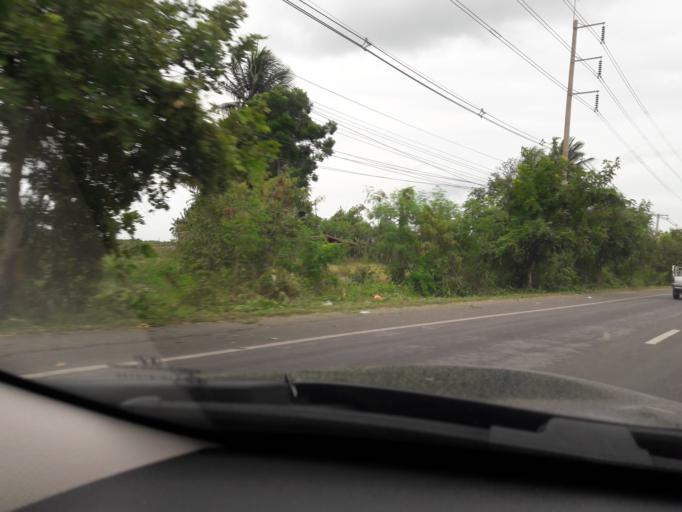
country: TH
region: Ratchaburi
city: Bang Phae
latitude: 13.6335
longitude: 99.9487
